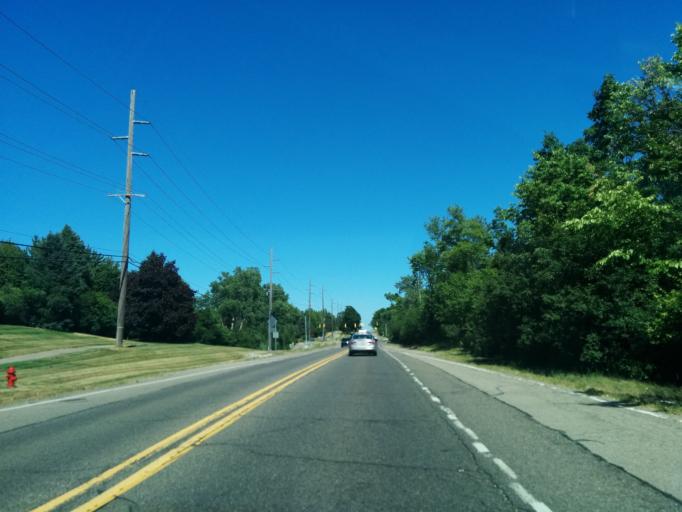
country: US
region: Michigan
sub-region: Oakland County
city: West Bloomfield Township
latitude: 42.5420
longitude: -83.3955
